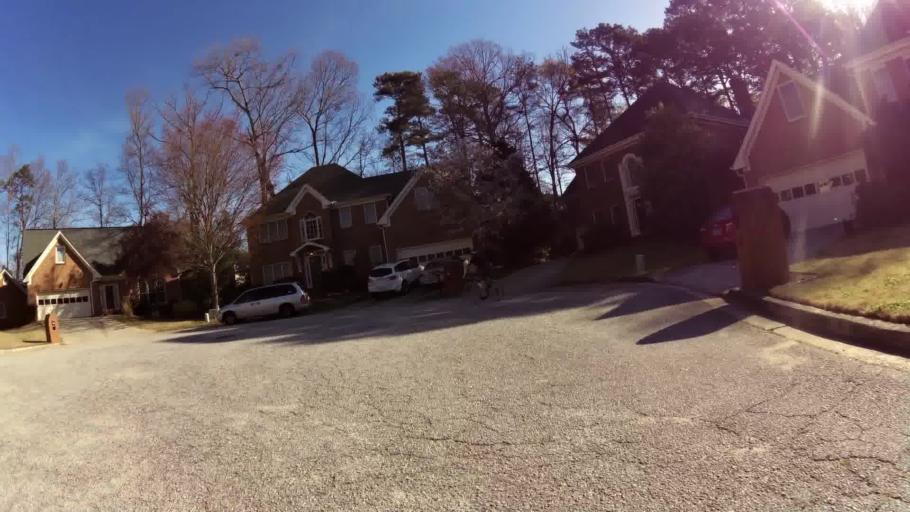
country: US
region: Georgia
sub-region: DeKalb County
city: Clarkston
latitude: 33.8343
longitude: -84.2698
